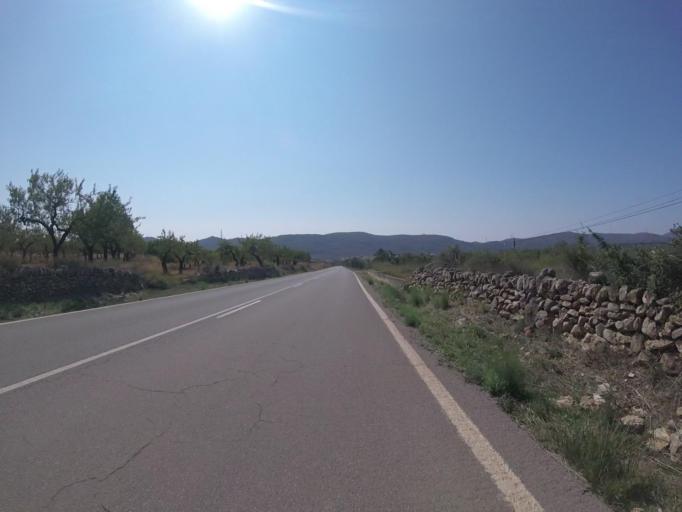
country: ES
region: Valencia
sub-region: Provincia de Castello
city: Adzaneta
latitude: 40.2300
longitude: -0.1761
